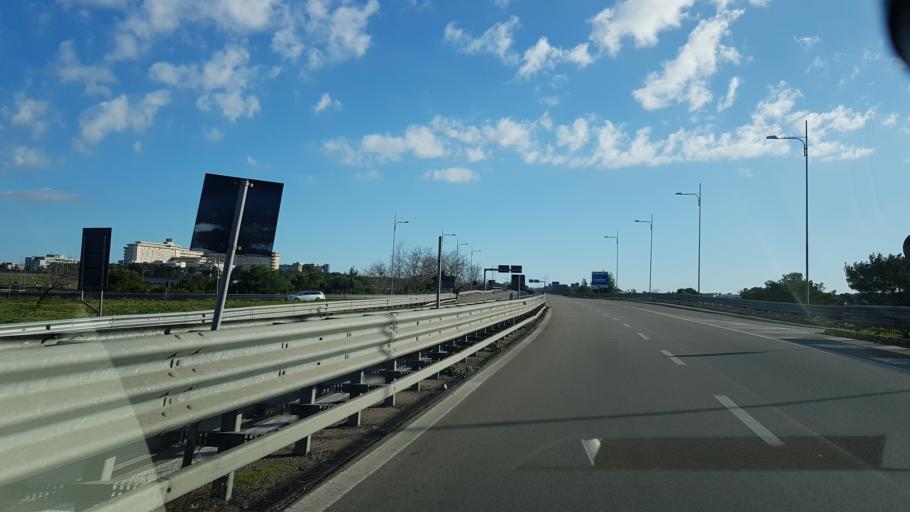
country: IT
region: Apulia
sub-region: Provincia di Lecce
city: Lequile
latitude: 40.3262
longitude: 18.1475
